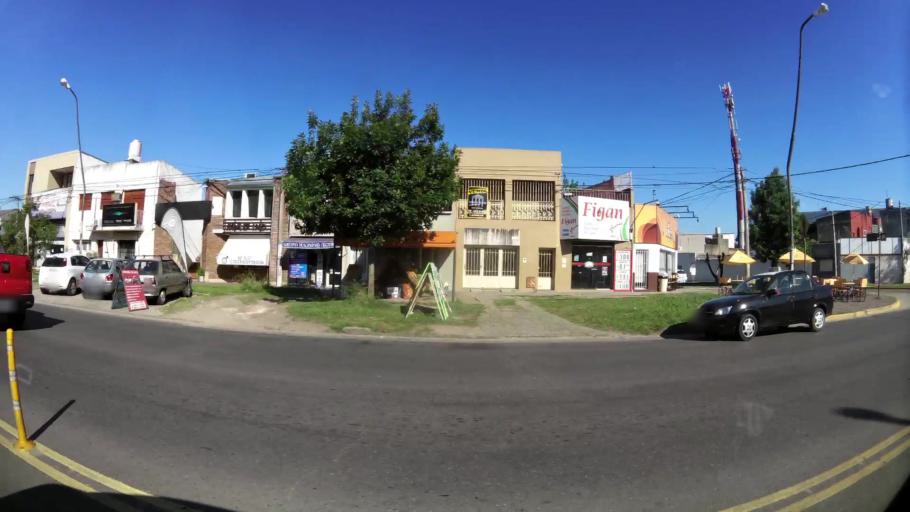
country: AR
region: Santa Fe
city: Santa Fe de la Vera Cruz
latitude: -31.6153
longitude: -60.6971
